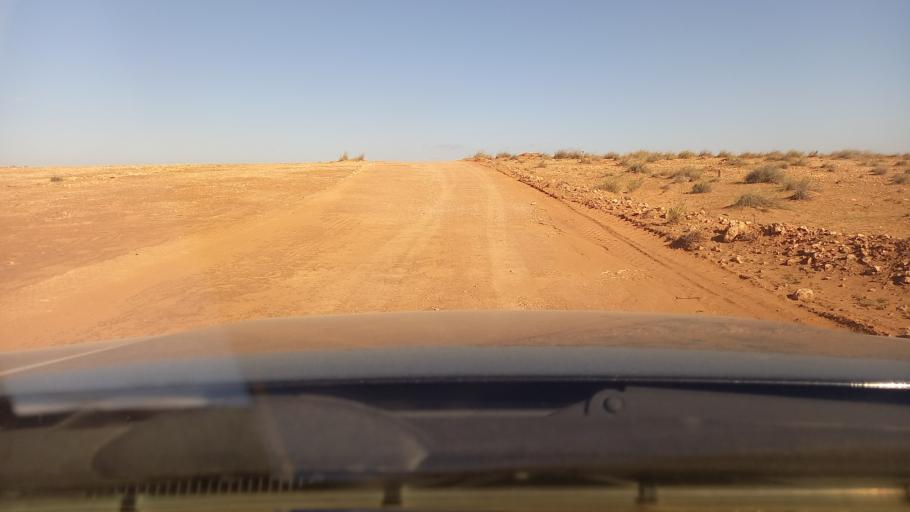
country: TN
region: Madanin
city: Medenine
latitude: 33.1729
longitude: 10.5271
